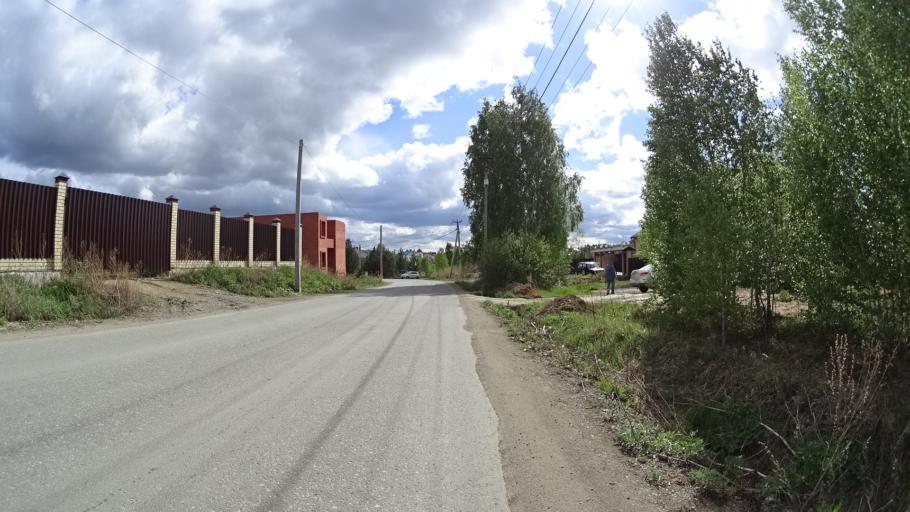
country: RU
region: Chelyabinsk
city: Sargazy
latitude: 55.1580
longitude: 61.2422
